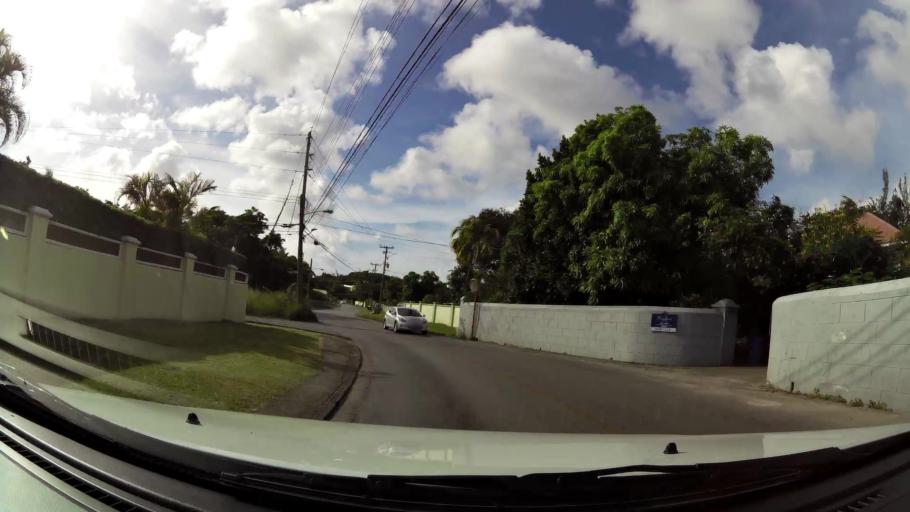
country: BB
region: Saint Michael
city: Bridgetown
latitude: 13.0774
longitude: -59.5863
